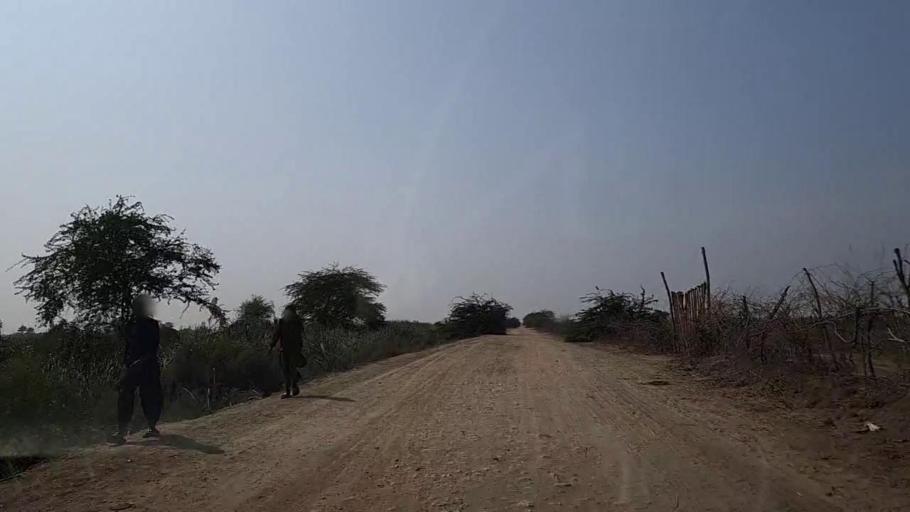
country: PK
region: Sindh
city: Gharo
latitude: 24.6844
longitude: 67.7457
